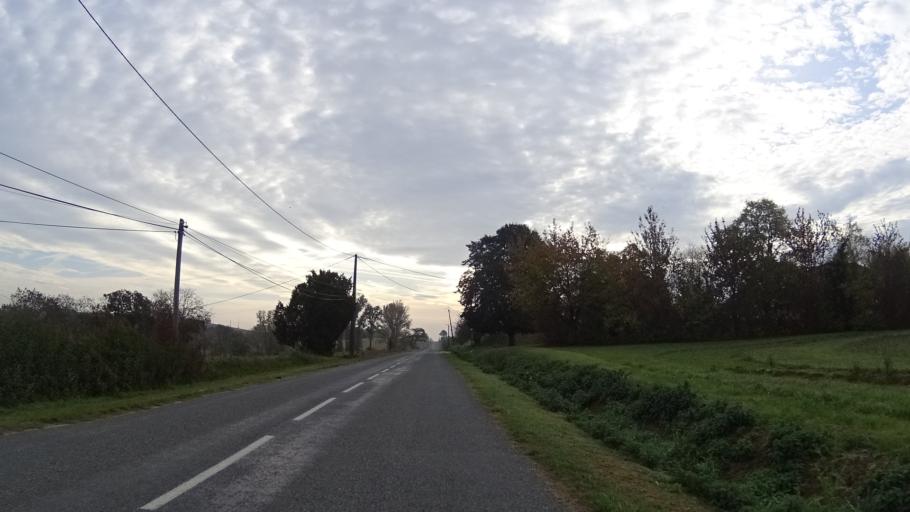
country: FR
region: Aquitaine
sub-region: Departement du Lot-et-Garonne
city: Laplume
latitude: 44.1015
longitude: 0.5547
